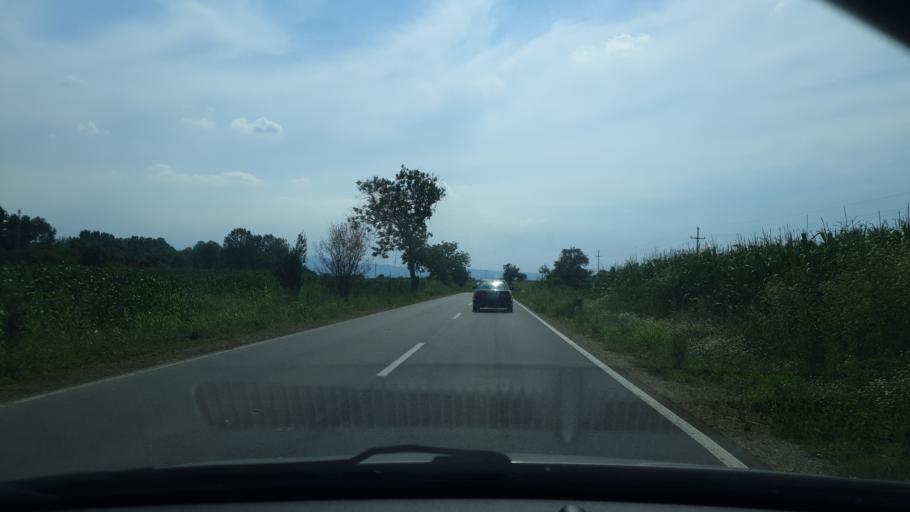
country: RS
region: Central Serbia
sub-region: Pomoravski Okrug
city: Cuprija
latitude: 43.9542
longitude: 21.4527
